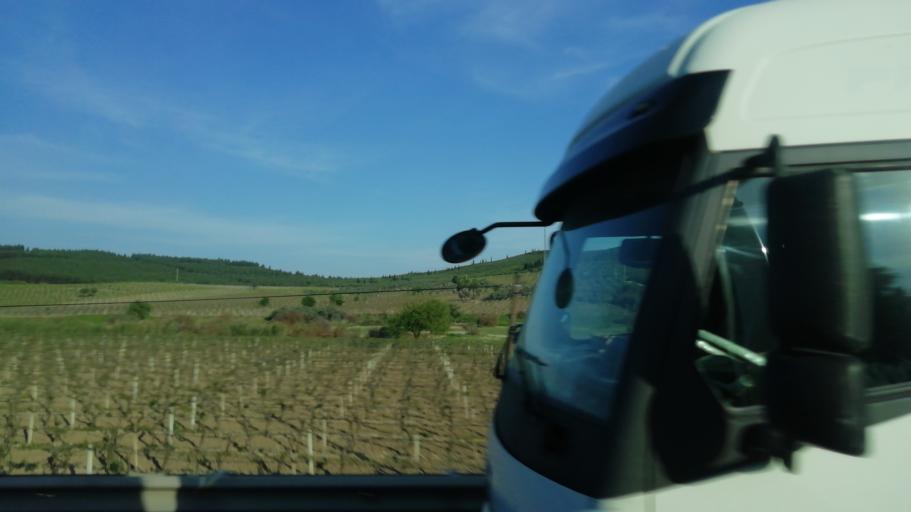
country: TR
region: Manisa
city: Halitpasa
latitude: 38.7949
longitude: 27.6844
